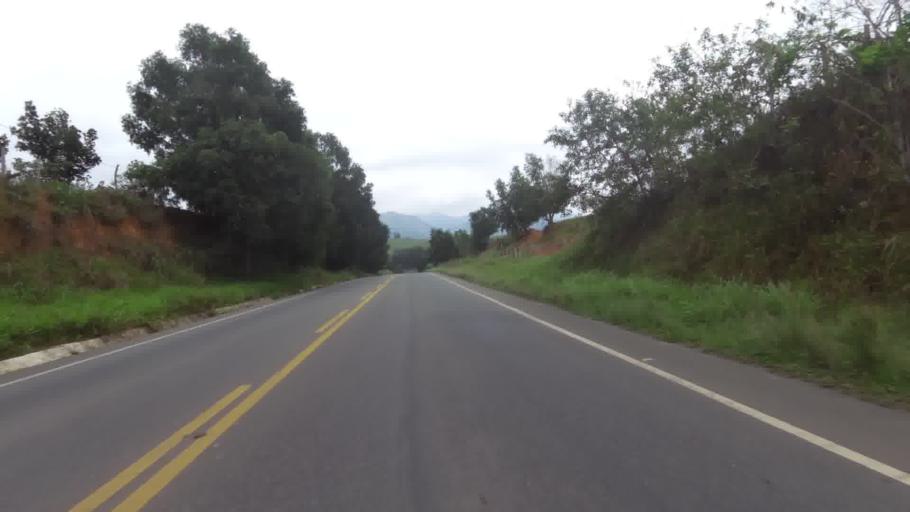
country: BR
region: Espirito Santo
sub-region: Iconha
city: Iconha
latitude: -20.7782
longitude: -40.7579
